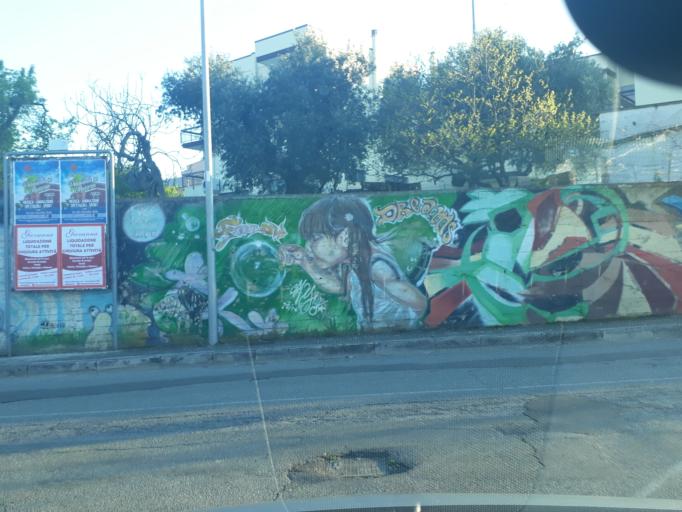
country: IT
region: Apulia
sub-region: Provincia di Bari
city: Locorotondo
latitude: 40.7596
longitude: 17.3254
